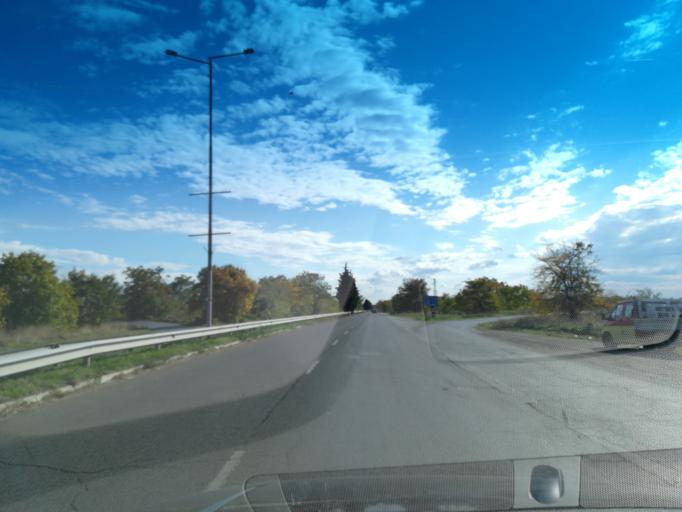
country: BG
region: Stara Zagora
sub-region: Obshtina Stara Zagora
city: Stara Zagora
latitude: 42.3937
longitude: 25.6460
